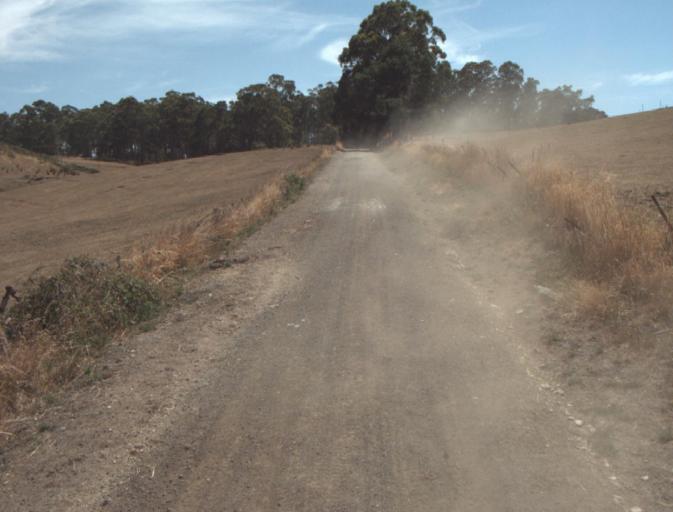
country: AU
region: Tasmania
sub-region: Launceston
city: Mayfield
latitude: -41.2523
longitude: 147.1736
